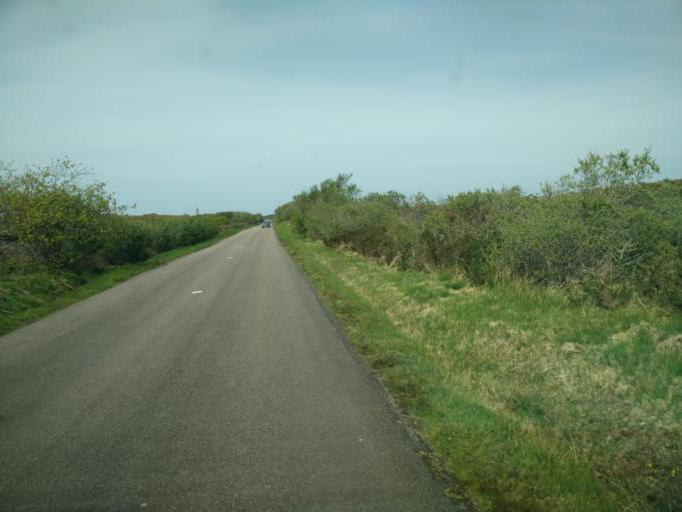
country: FR
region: Brittany
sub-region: Departement des Cotes-d'Armor
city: Saint-Cast-le-Guildo
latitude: 48.6703
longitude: -2.3195
